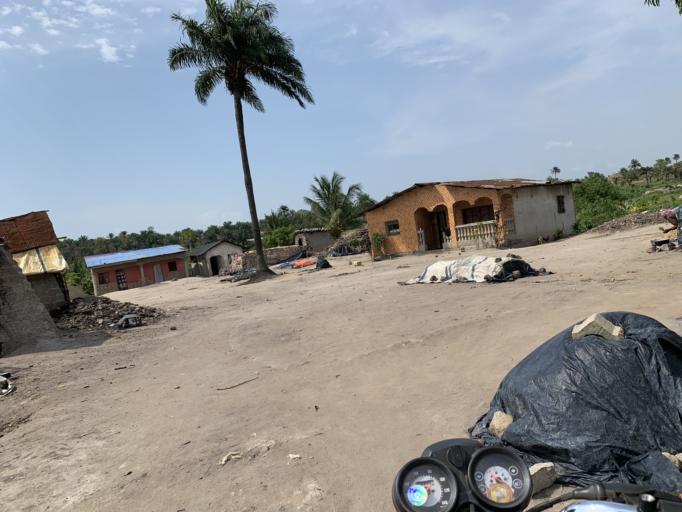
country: SL
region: Western Area
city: Waterloo
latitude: 8.3503
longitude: -13.0528
